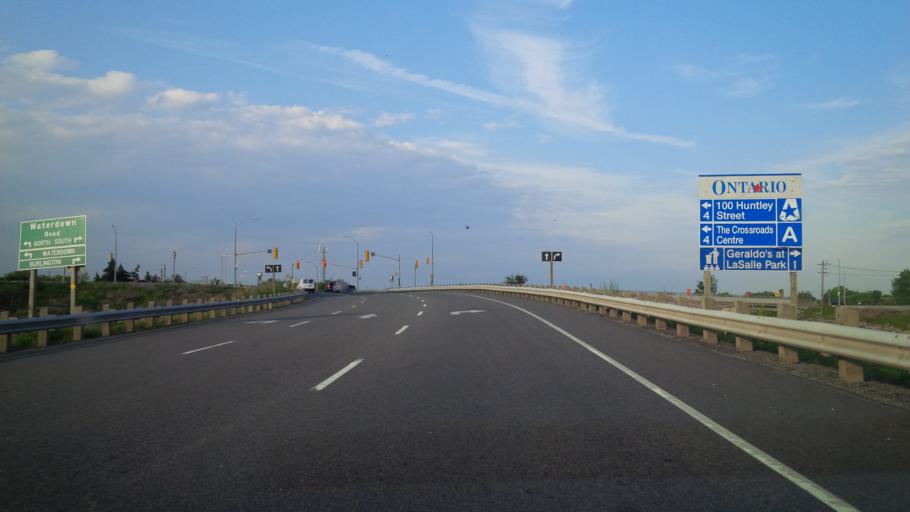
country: CA
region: Ontario
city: Hamilton
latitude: 43.3106
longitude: -79.8605
